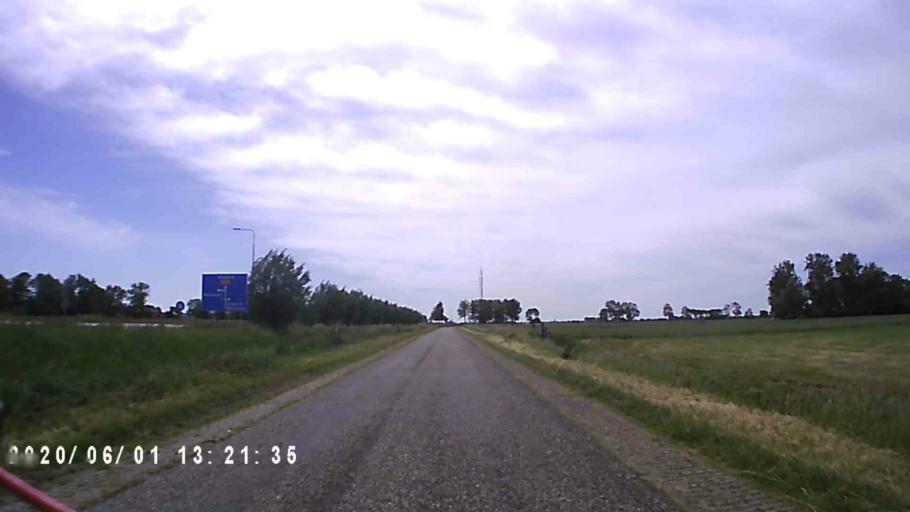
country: NL
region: Friesland
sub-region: Gemeente Littenseradiel
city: Wommels
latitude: 53.1112
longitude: 5.5831
